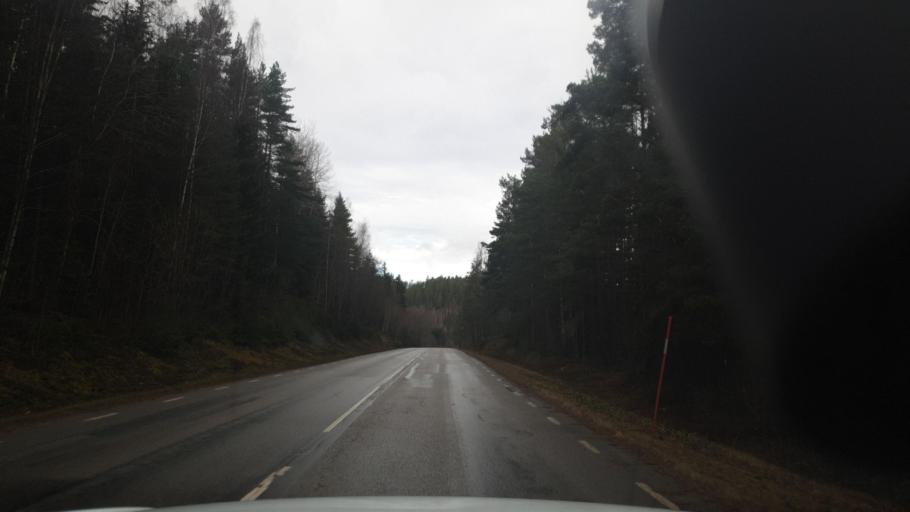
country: SE
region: Vaermland
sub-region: Arvika Kommun
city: Arvika
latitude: 59.7141
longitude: 12.6309
